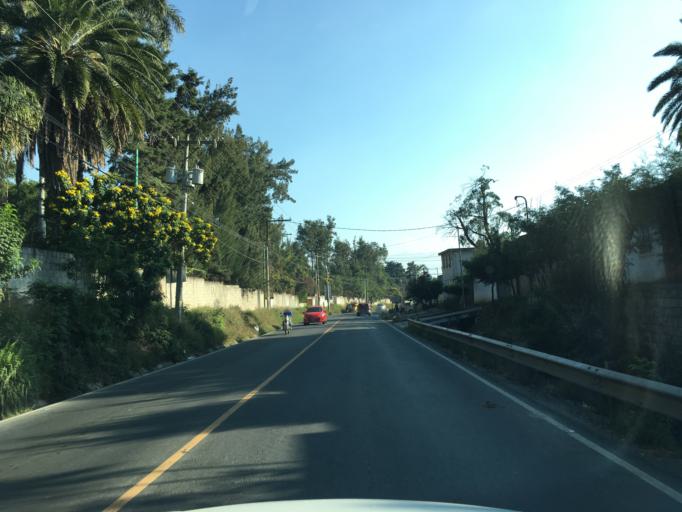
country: GT
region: Guatemala
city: Villa Nueva
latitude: 14.5394
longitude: -90.6151
